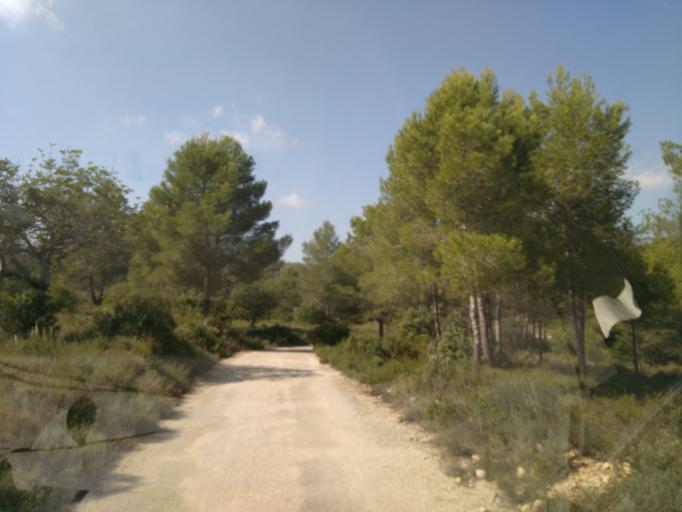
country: ES
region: Valencia
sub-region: Provincia de Valencia
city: Tous
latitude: 39.1771
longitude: -0.6201
